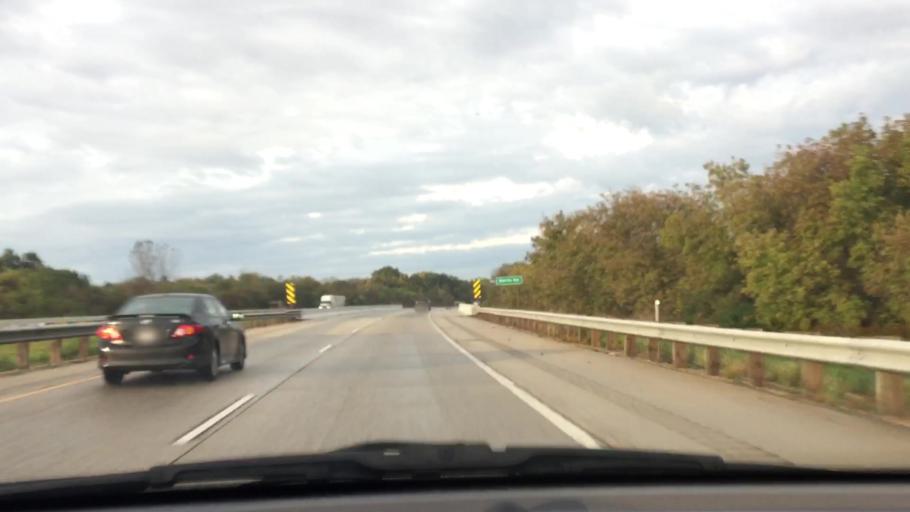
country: US
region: Wisconsin
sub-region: Walworth County
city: Darien
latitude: 42.5848
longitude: -88.7601
